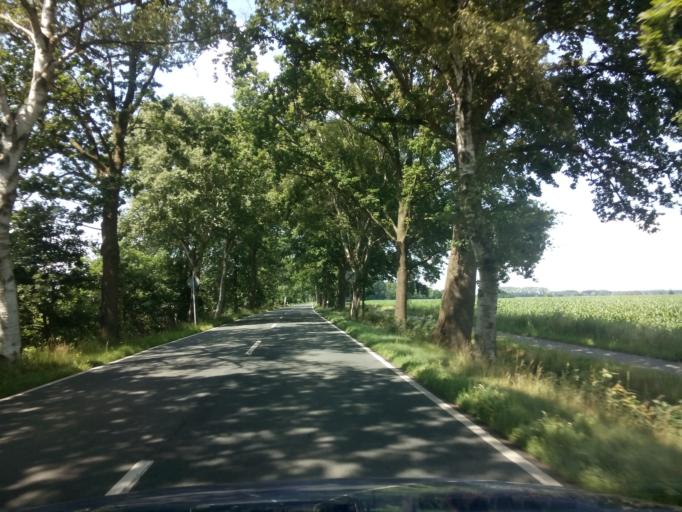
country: DE
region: Lower Saxony
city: Worpswede
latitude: 53.2561
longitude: 8.9404
